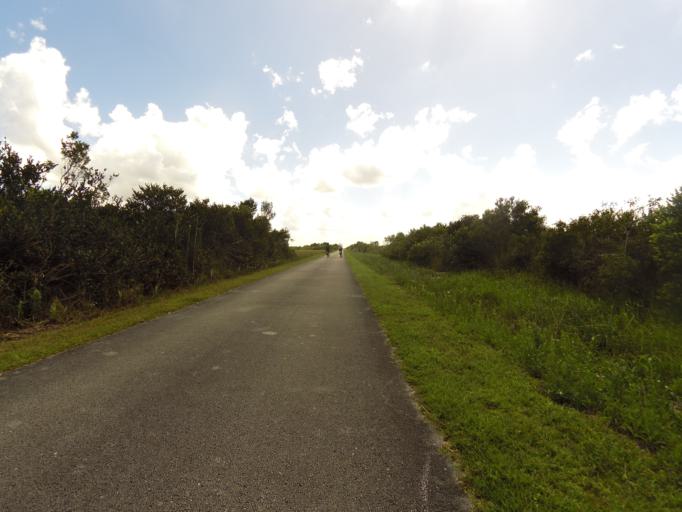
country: US
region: Florida
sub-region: Miami-Dade County
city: The Hammocks
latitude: 25.7130
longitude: -80.7667
